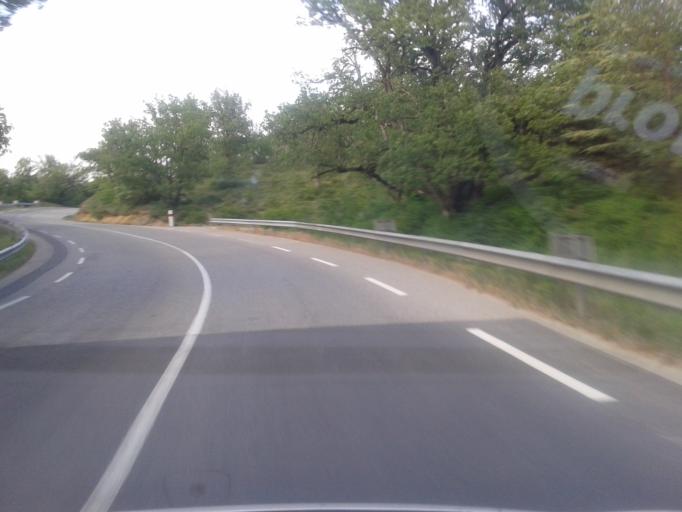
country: FR
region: Provence-Alpes-Cote d'Azur
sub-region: Departement du Var
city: Vinon-sur-Verdon
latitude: 43.7141
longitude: 5.7784
